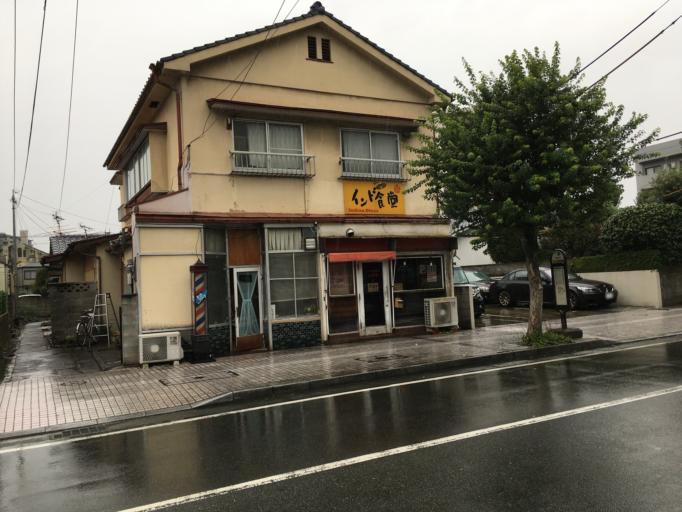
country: JP
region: Kumamoto
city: Kumamoto
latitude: 32.7983
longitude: 130.7245
